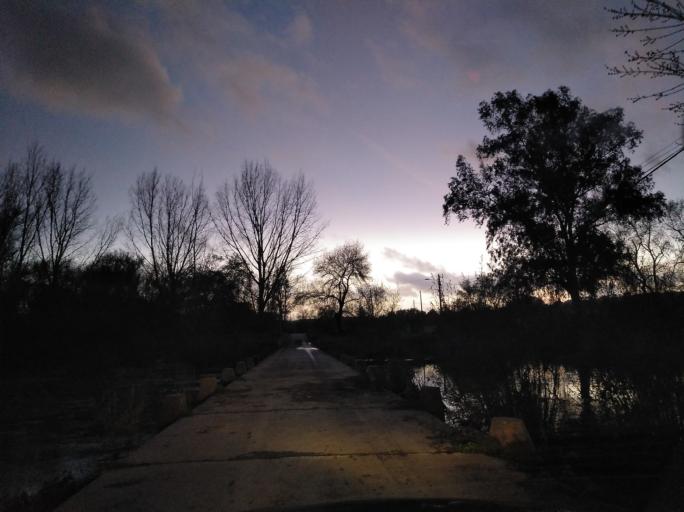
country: PT
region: Portalegre
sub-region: Campo Maior
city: Campo Maior
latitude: 39.0805
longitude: -7.0181
